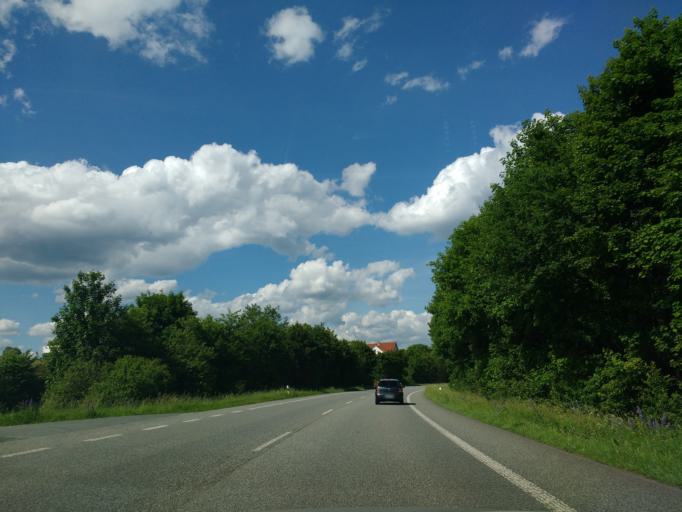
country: DE
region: Hesse
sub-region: Regierungsbezirk Giessen
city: Breidenbach
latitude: 50.9066
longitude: 8.4536
